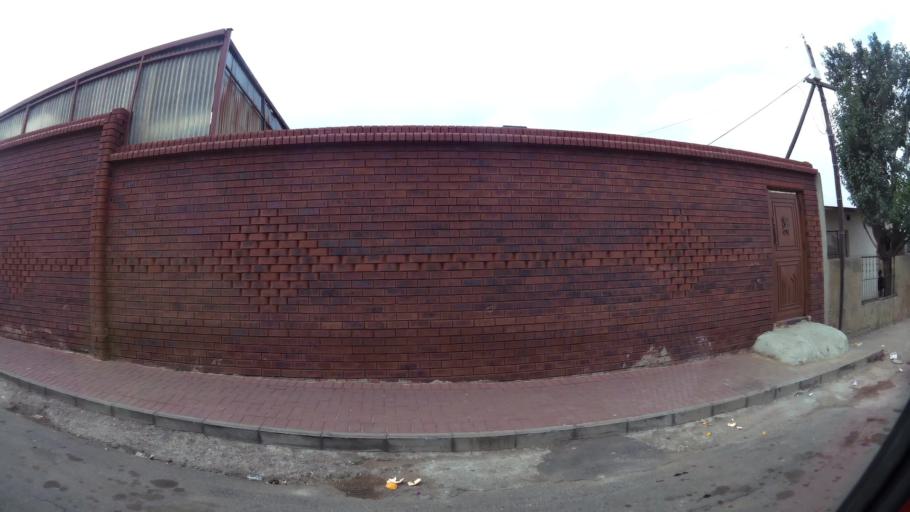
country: ZA
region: Gauteng
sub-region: City of Johannesburg Metropolitan Municipality
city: Soweto
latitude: -26.2364
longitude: 27.8631
